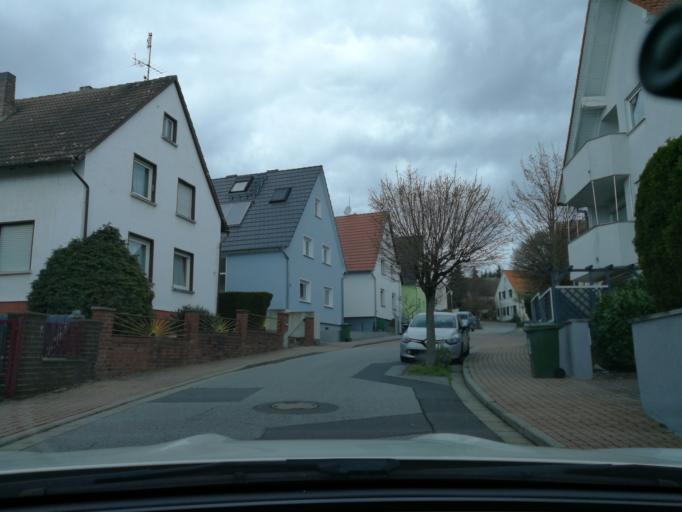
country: DE
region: Hesse
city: Reinheim
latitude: 49.8221
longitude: 8.8291
